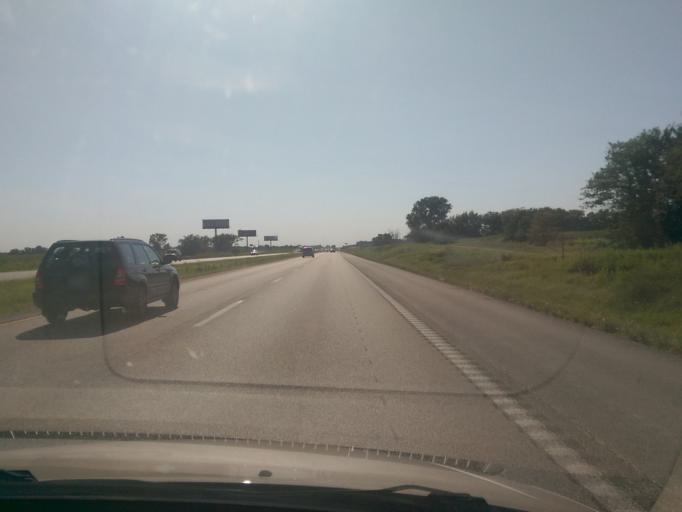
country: US
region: Missouri
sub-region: Saline County
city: Sweet Springs
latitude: 38.9738
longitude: -93.3375
